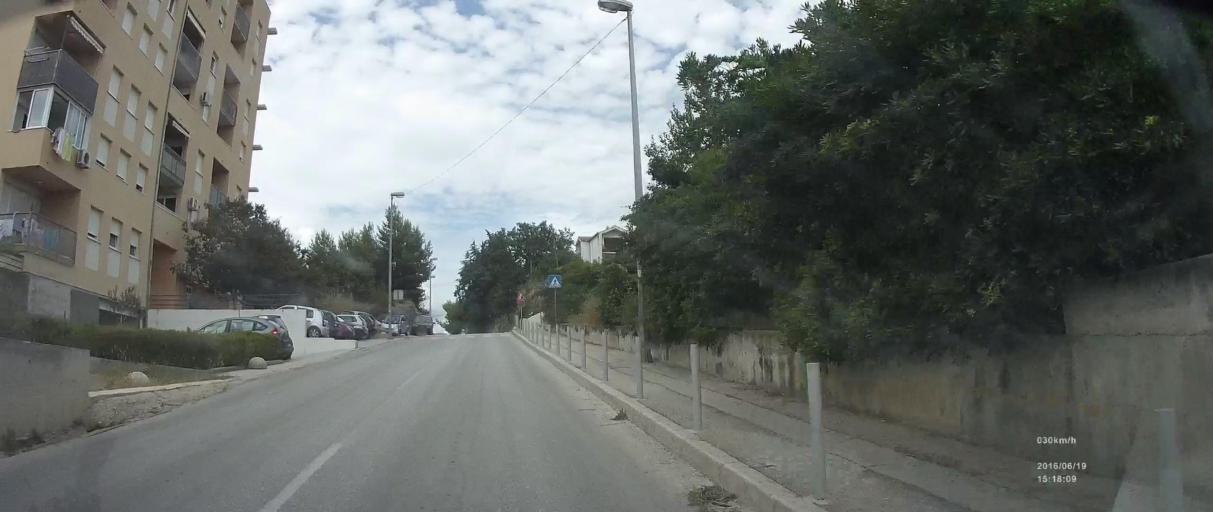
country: HR
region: Splitsko-Dalmatinska
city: Kamen
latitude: 43.5071
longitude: 16.4961
